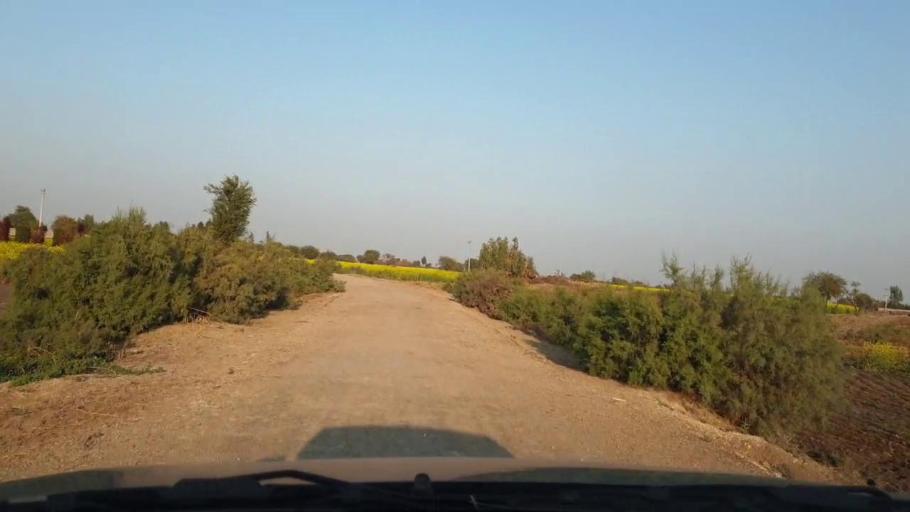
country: PK
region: Sindh
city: Jhol
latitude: 25.9331
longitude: 68.9329
